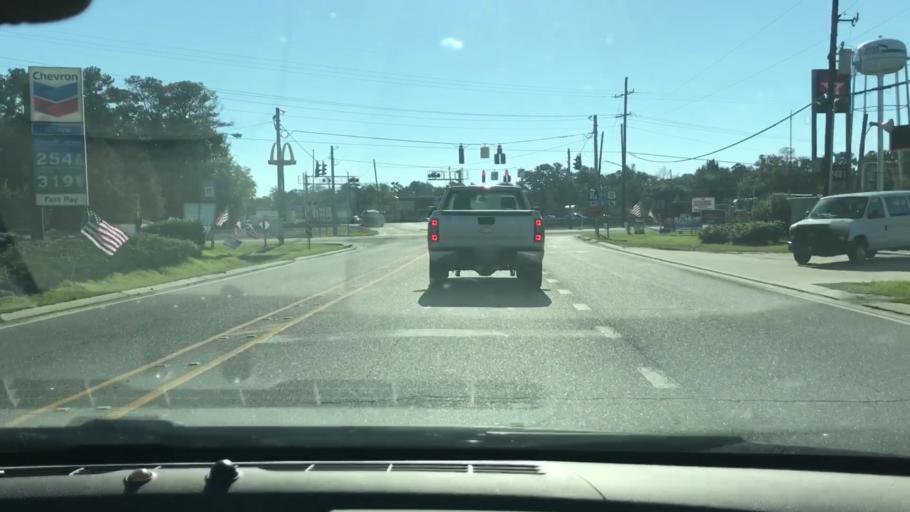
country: US
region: Louisiana
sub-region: Saint Tammany Parish
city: Pearl River
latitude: 30.3605
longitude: -89.7515
